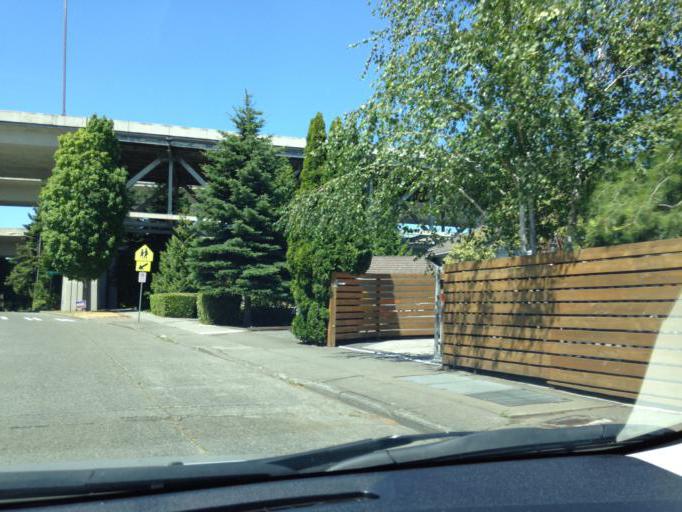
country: US
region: Washington
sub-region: King County
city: Seattle
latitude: 47.5894
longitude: -122.2862
